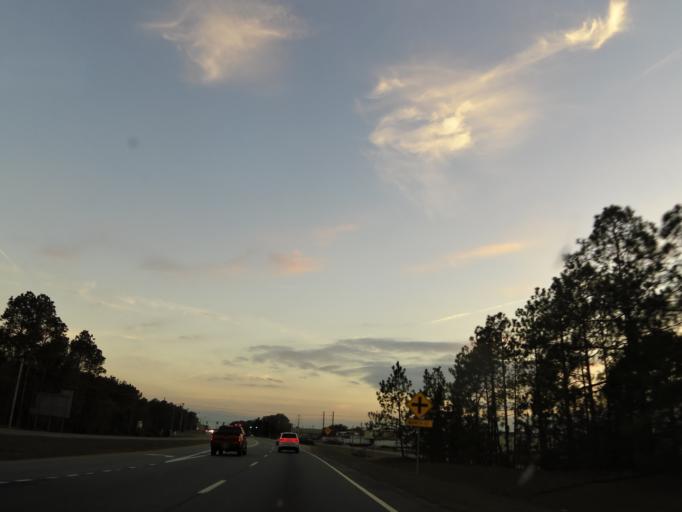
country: US
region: Georgia
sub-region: Dougherty County
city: Albany
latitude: 31.5586
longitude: -84.1148
